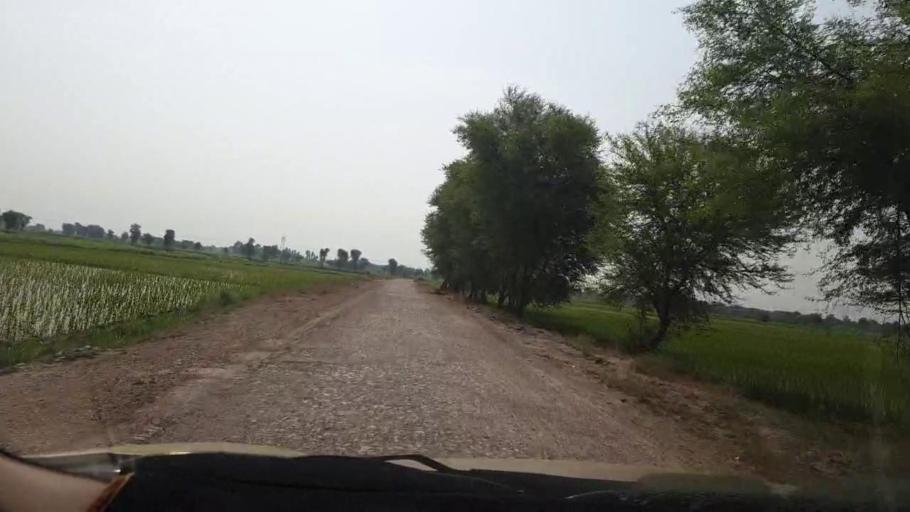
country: PK
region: Sindh
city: Goth Garelo
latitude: 27.4381
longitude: 68.0405
